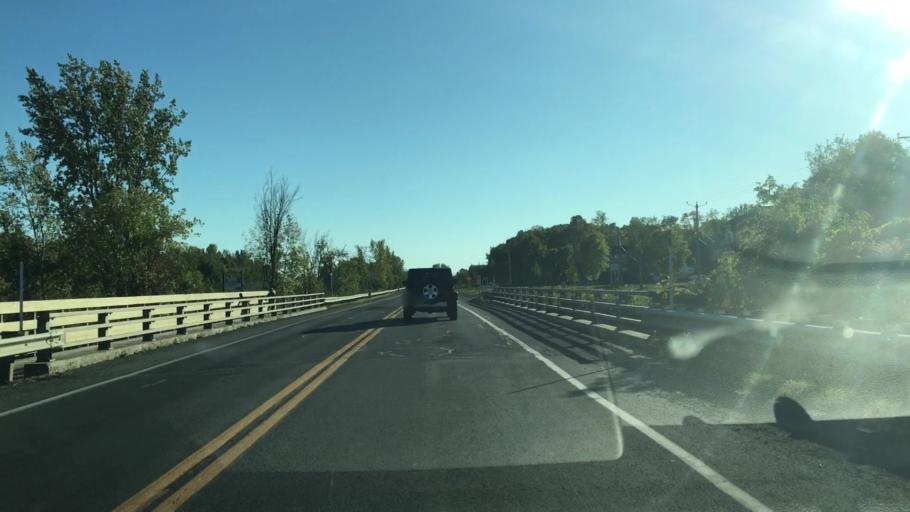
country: CA
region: Quebec
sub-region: Monteregie
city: Les Coteaux
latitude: 45.2908
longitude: -74.1838
